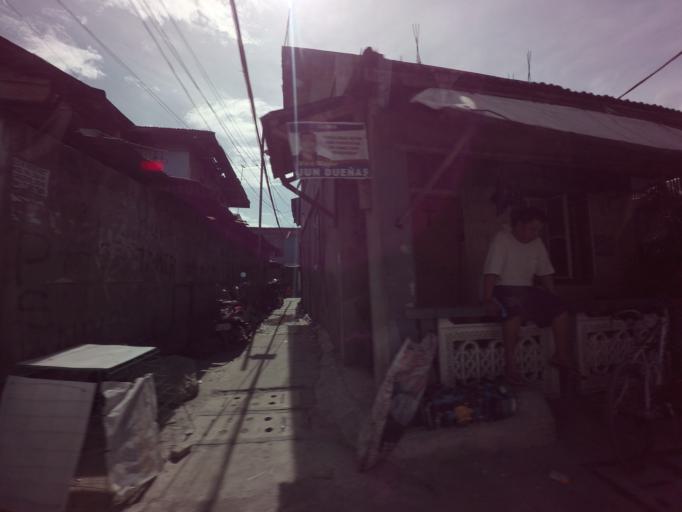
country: PH
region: Calabarzon
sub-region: Province of Rizal
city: Taguig
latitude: 14.5381
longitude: 121.0977
